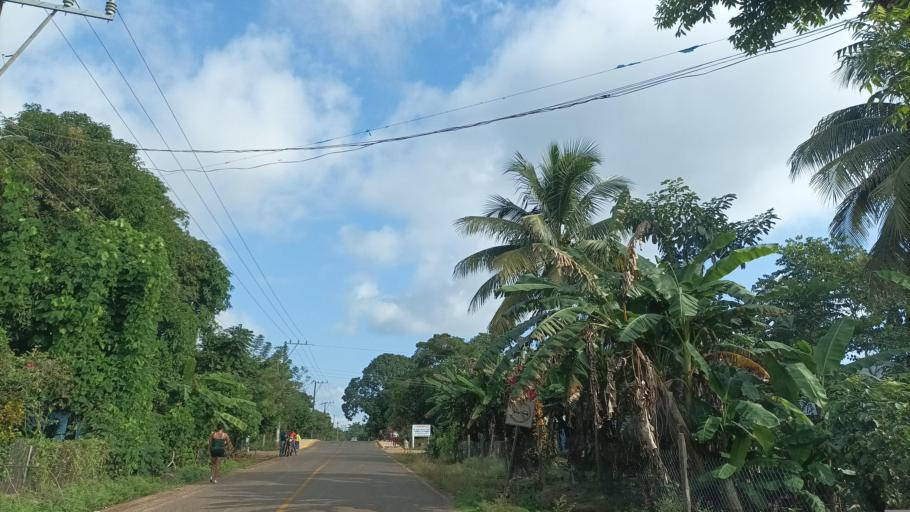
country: MX
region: Veracruz
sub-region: Pajapan
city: Pajapan
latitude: 18.1816
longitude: -94.6734
